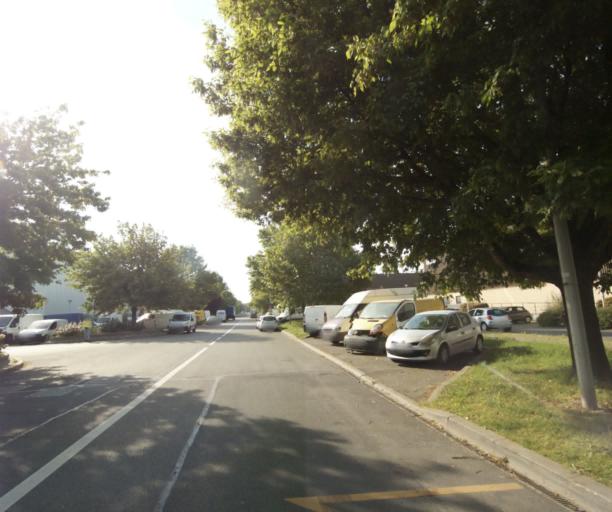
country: FR
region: Ile-de-France
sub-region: Departement des Hauts-de-Seine
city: Bois-Colombes
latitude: 48.9412
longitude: 2.2776
